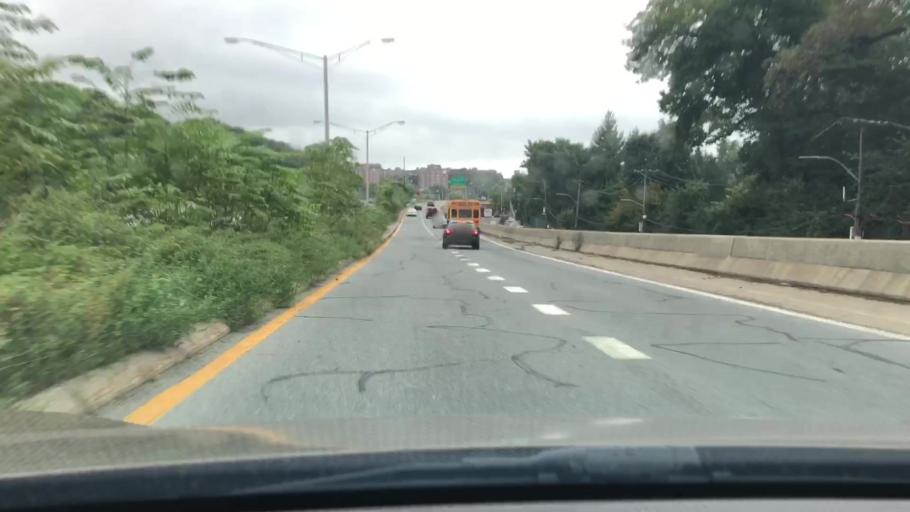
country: US
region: New York
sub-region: Westchester County
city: Bronxville
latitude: 40.9291
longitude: -73.8460
